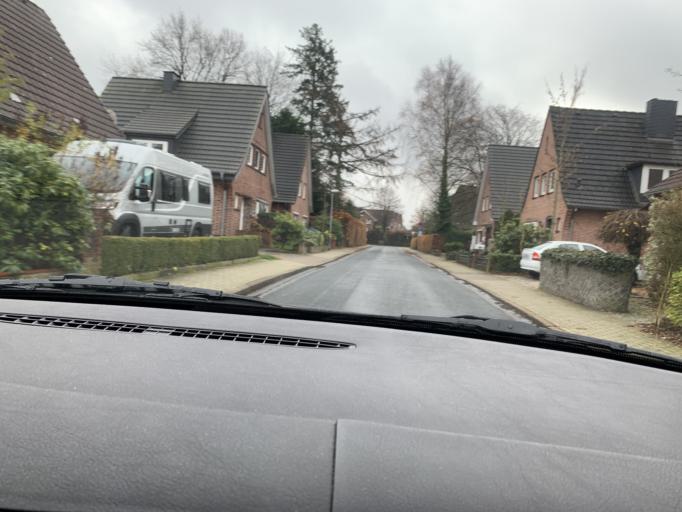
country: DE
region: Schleswig-Holstein
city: Wesseln
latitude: 54.2007
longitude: 9.0828
